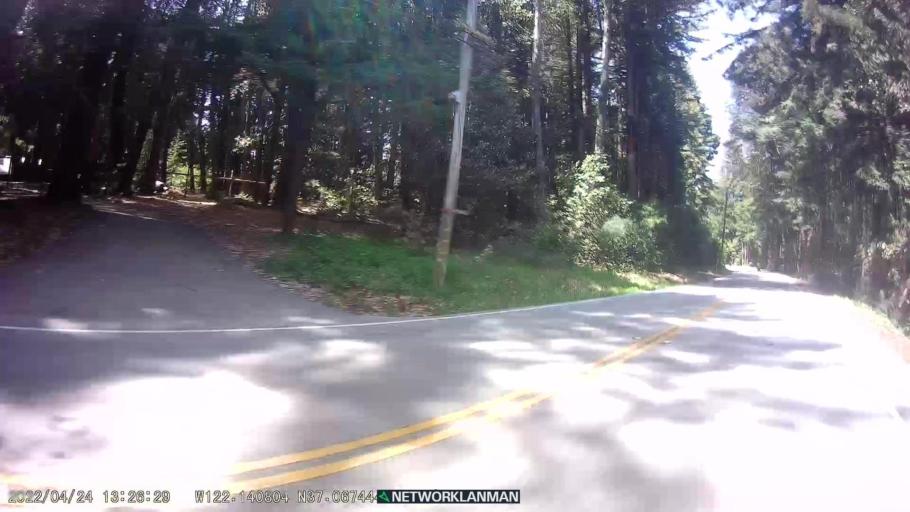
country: US
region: California
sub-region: Santa Cruz County
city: Bonny Doon
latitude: 37.0674
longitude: -122.1409
